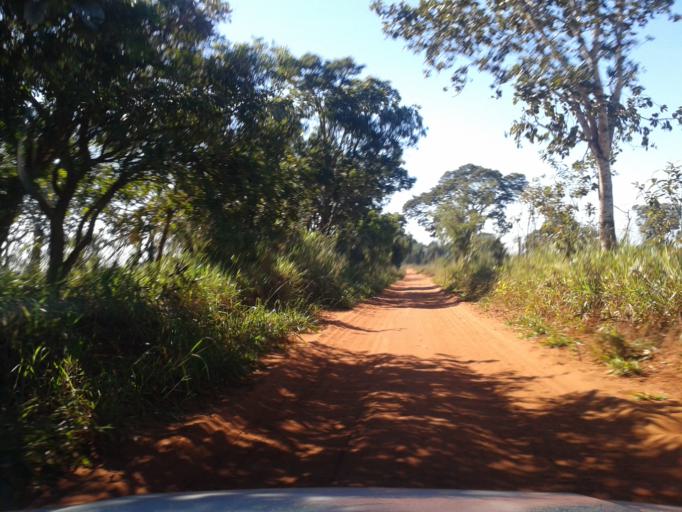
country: BR
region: Minas Gerais
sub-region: Ituiutaba
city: Ituiutaba
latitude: -19.0942
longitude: -49.7991
